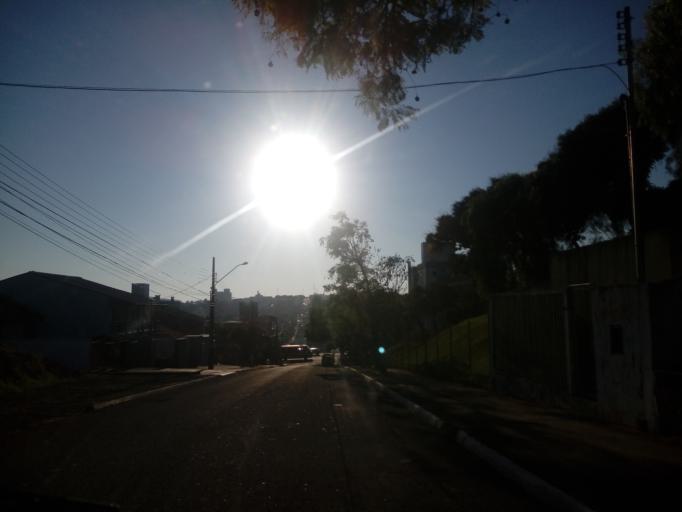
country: BR
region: Santa Catarina
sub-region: Chapeco
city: Chapeco
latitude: -27.1127
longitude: -52.6113
